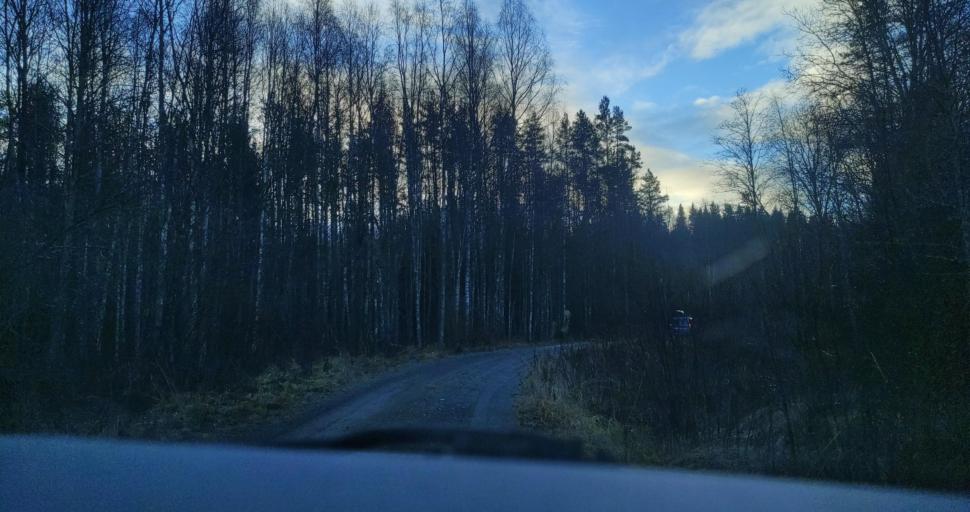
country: RU
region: Republic of Karelia
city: Pitkyaranta
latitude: 61.7341
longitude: 31.3729
